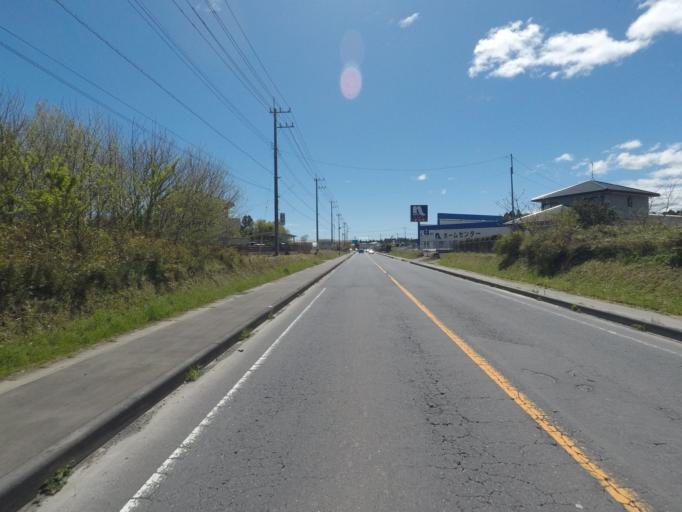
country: JP
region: Ibaraki
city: Ishioka
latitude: 36.0933
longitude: 140.3023
